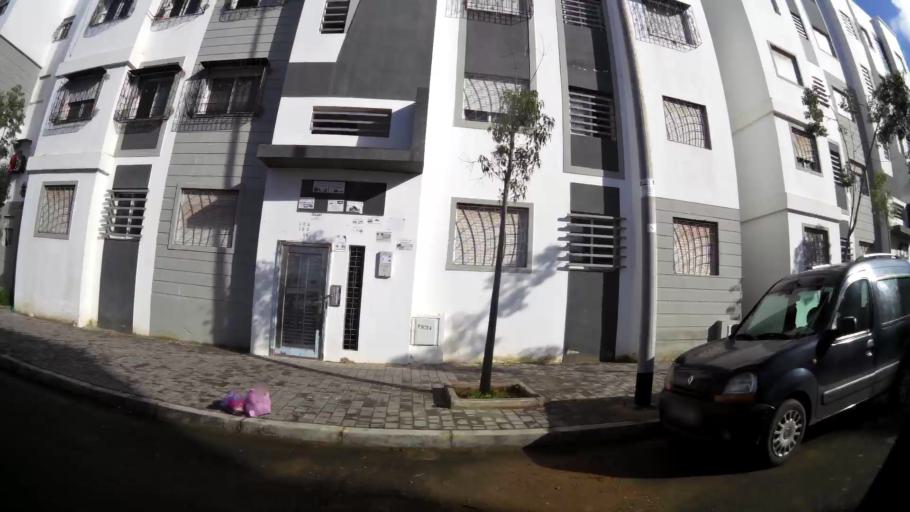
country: MA
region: Grand Casablanca
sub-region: Casablanca
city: Casablanca
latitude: 33.5539
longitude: -7.7044
